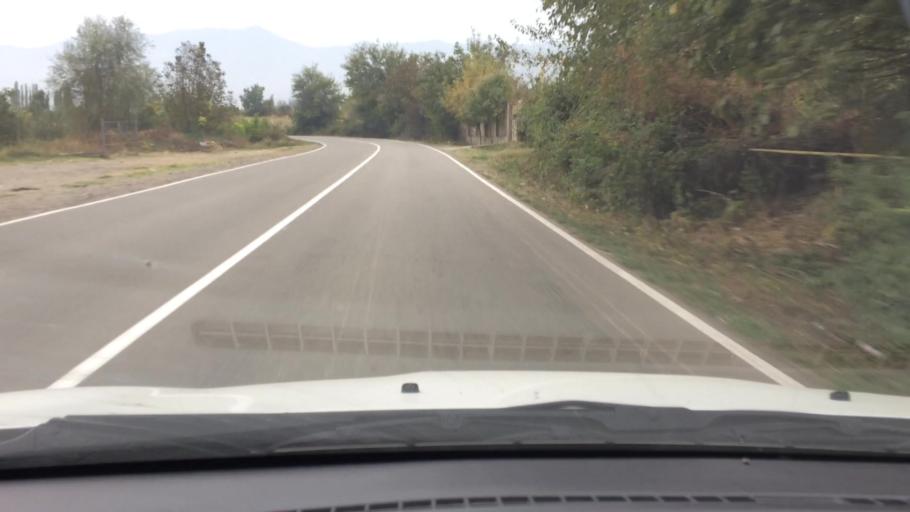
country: AM
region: Tavush
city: Bagratashen
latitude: 41.2596
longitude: 44.7962
